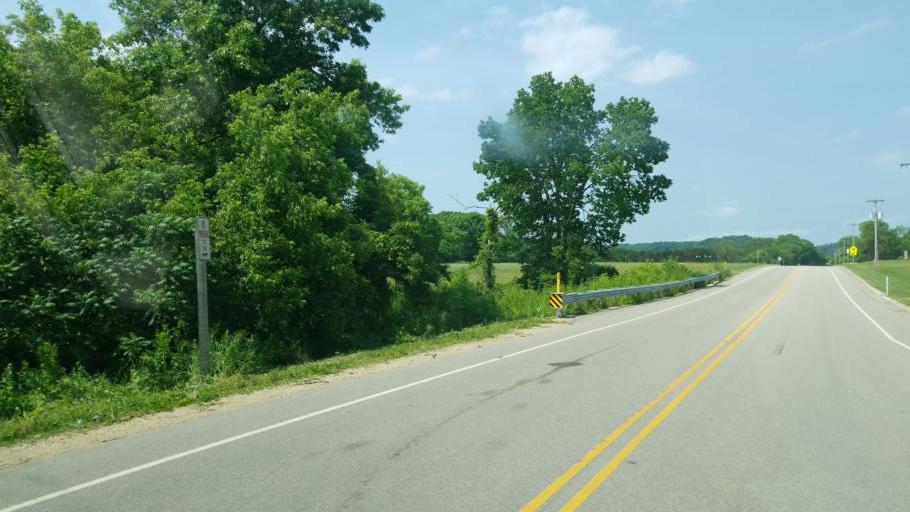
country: US
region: Wisconsin
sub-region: Vernon County
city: Viroqua
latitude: 43.4926
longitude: -90.6799
